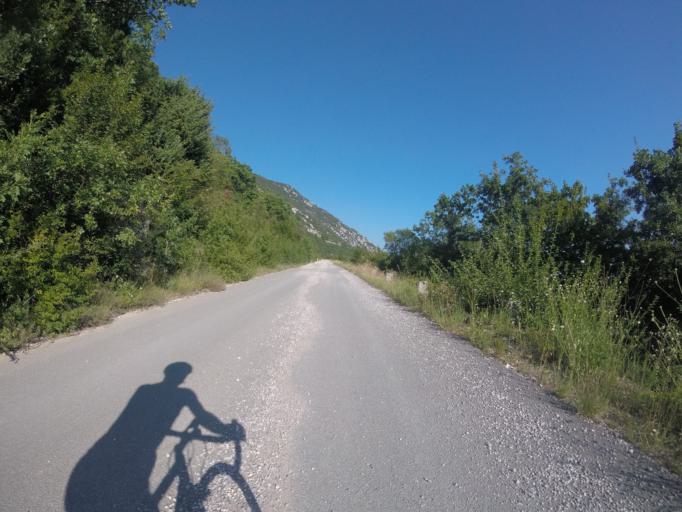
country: HR
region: Primorsko-Goranska
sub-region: Grad Crikvenica
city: Jadranovo
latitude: 45.2574
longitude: 14.6227
